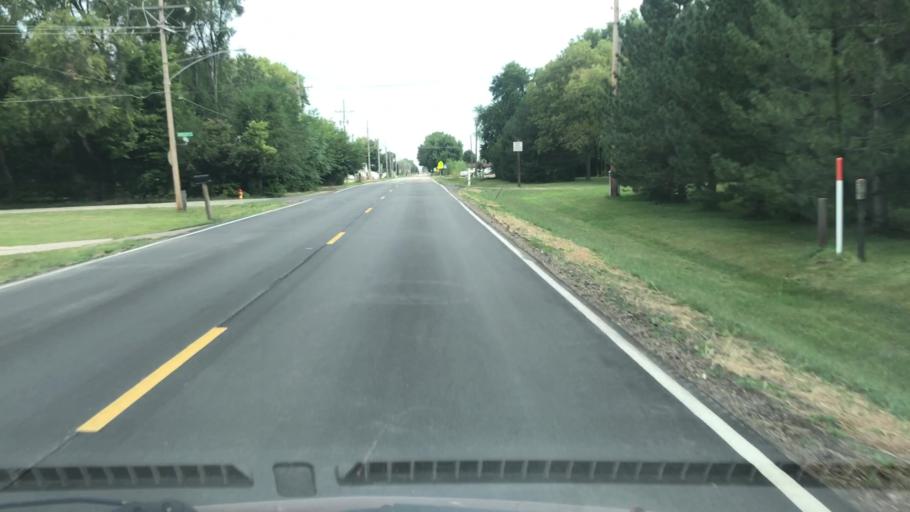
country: US
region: Nebraska
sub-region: Hall County
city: Grand Island
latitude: 40.9280
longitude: -98.3015
